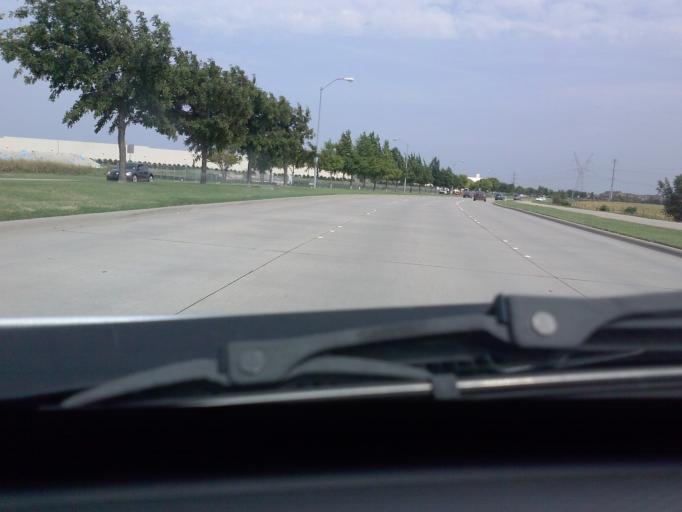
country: US
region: Texas
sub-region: Denton County
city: The Colony
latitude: 33.0650
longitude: -96.8155
